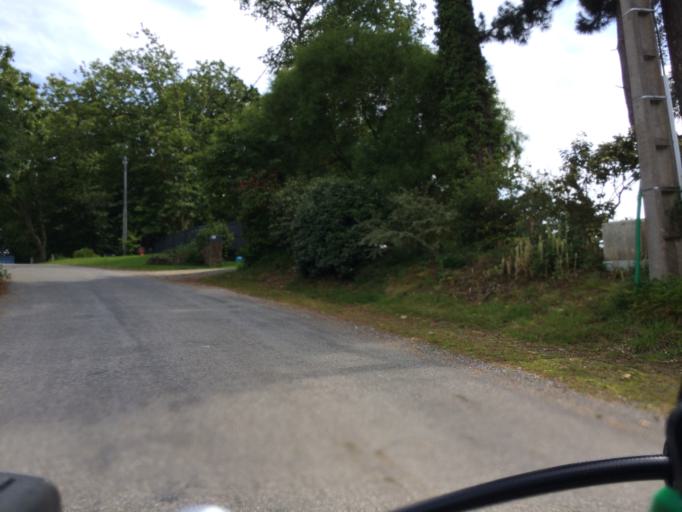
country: FR
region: Brittany
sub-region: Departement du Finistere
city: Logonna-Daoulas
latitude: 48.3189
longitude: -4.2854
